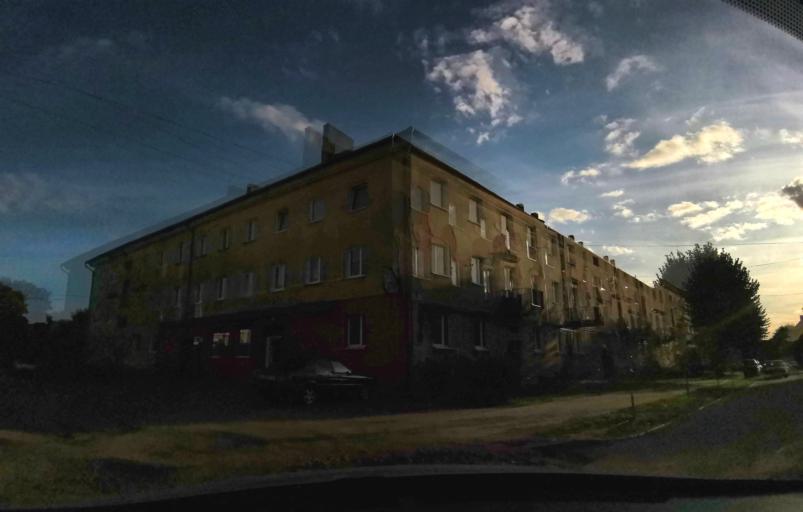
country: RU
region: Kaliningrad
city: Chernyakhovsk
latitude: 54.6319
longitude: 21.8245
